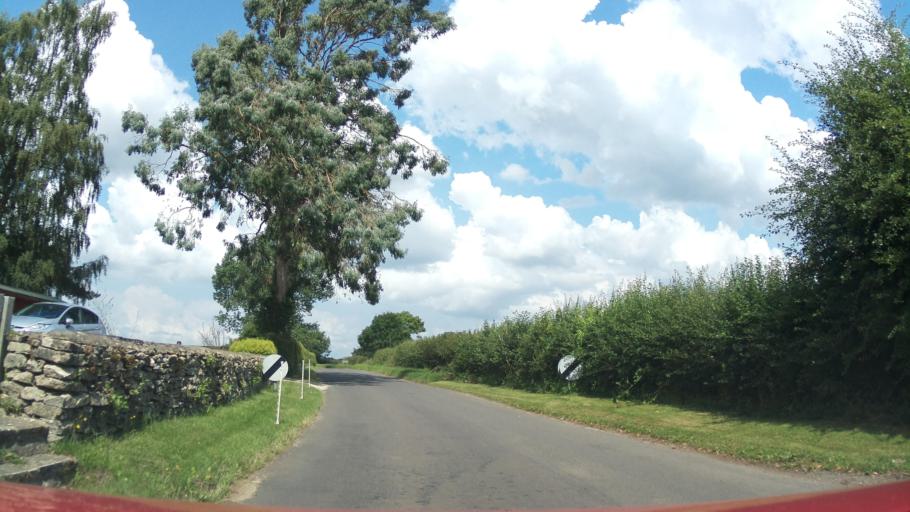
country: GB
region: England
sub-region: Wiltshire
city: Charlton
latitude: 51.6031
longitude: -2.0499
